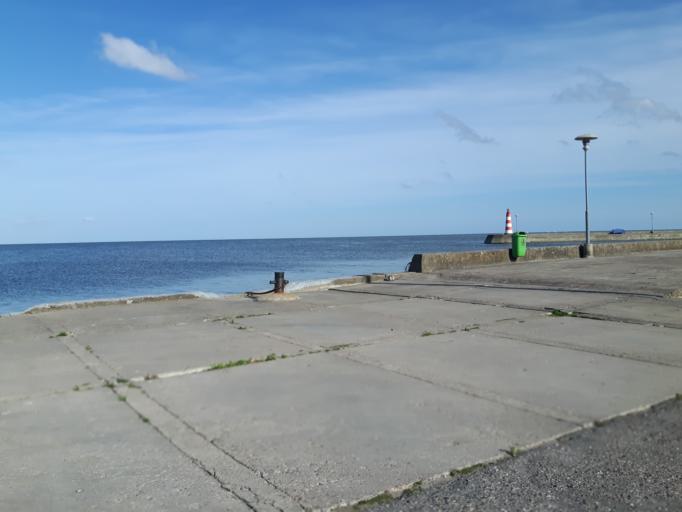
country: LT
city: Nida
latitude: 55.3025
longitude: 21.0104
